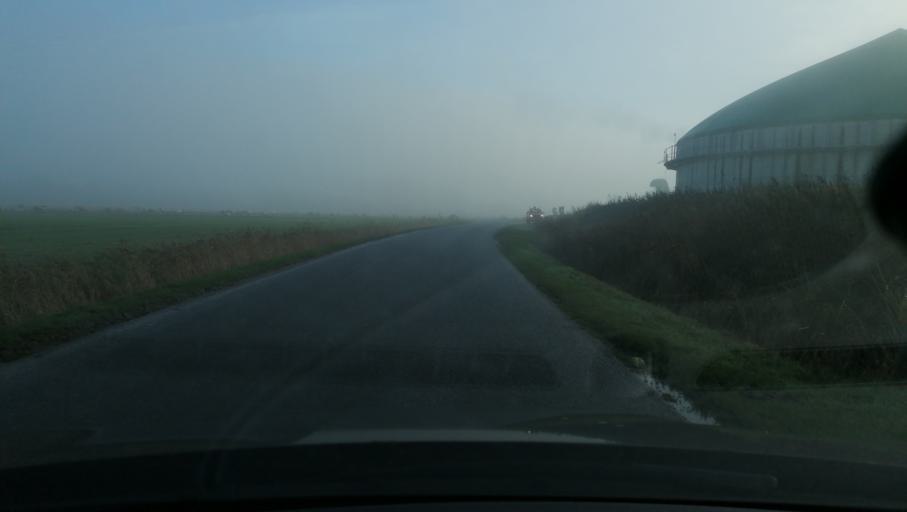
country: DE
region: Schleswig-Holstein
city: Meldorf
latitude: 54.0991
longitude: 9.0550
